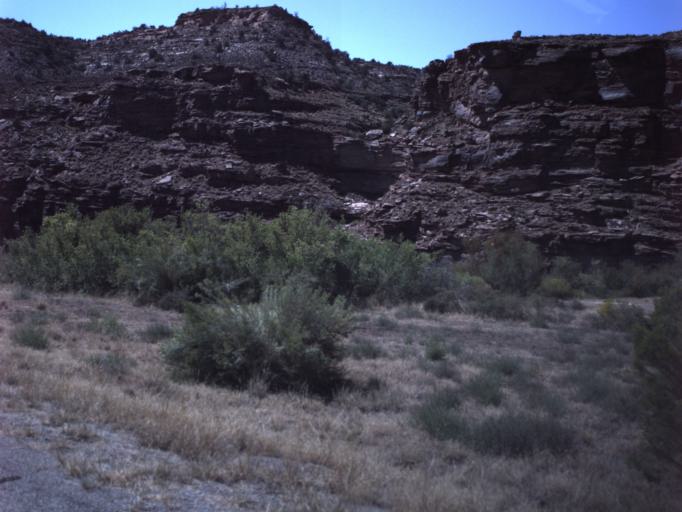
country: US
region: Utah
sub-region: Grand County
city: Moab
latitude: 38.8086
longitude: -109.3143
